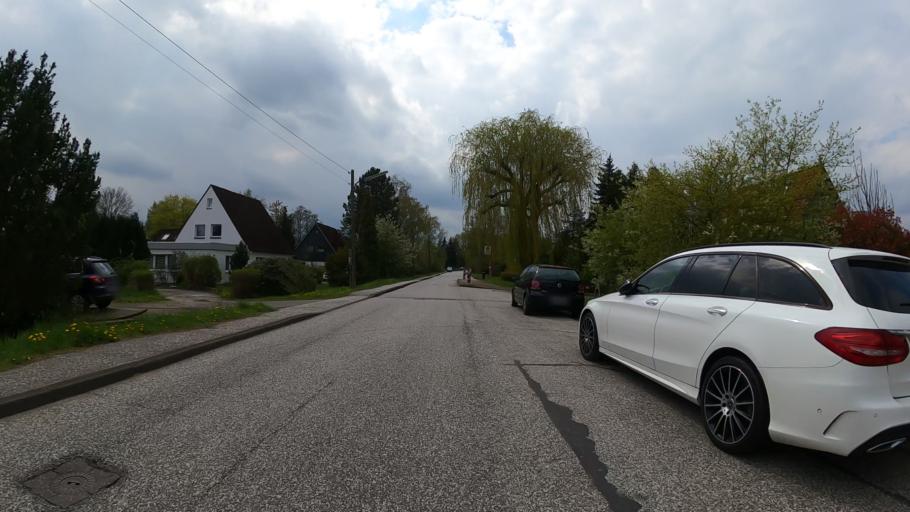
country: DE
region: Schleswig-Holstein
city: Oststeinbek
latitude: 53.4891
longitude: 10.1195
